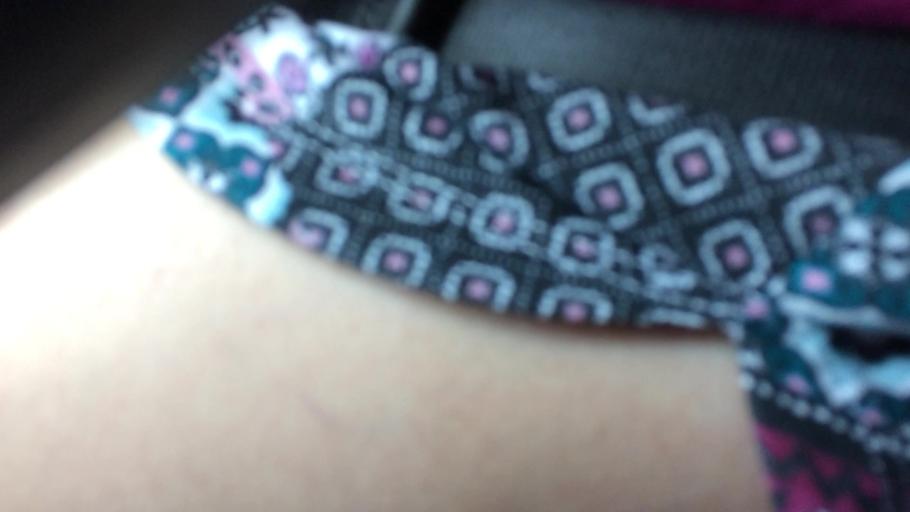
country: US
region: New Mexico
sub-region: Colfax County
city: Springer
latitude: 36.3685
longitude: -104.6028
